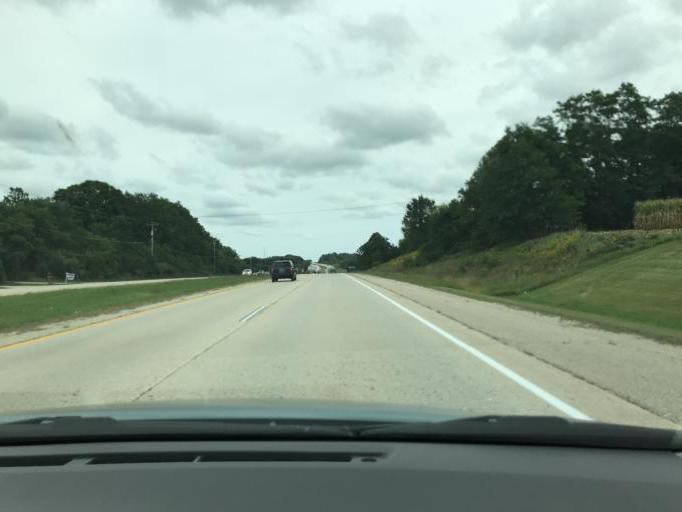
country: US
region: Wisconsin
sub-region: Kenosha County
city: Bristol
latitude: 42.5680
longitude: -88.0761
